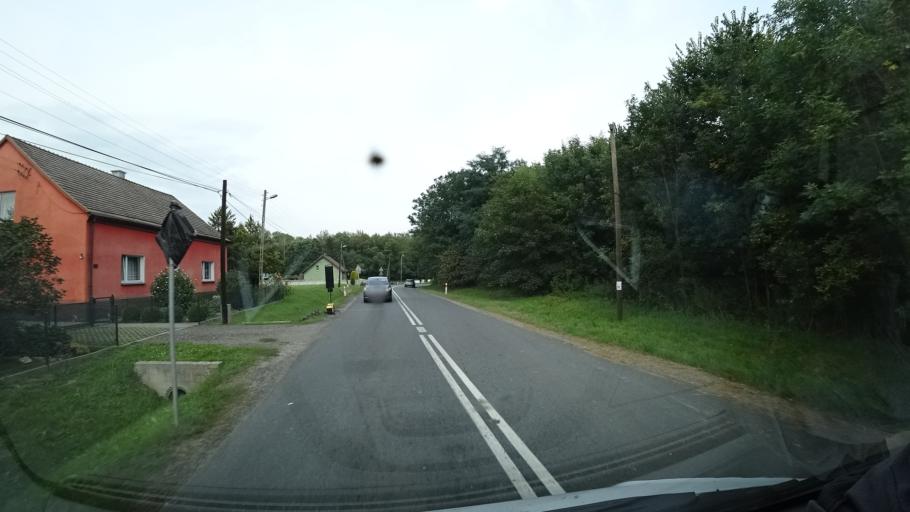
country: PL
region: Silesian Voivodeship
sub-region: Powiat gliwicki
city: Pyskowice
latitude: 50.3927
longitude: 18.5992
